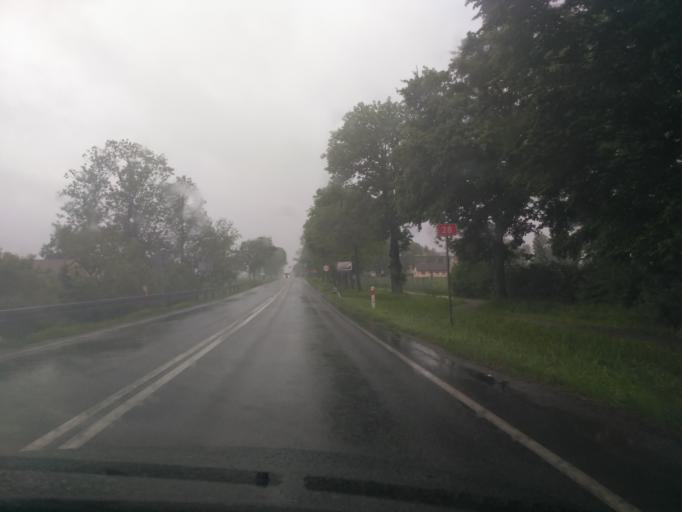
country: PL
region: Subcarpathian Voivodeship
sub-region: Powiat jasielski
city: Tarnowiec
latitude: 49.7609
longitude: 21.5936
